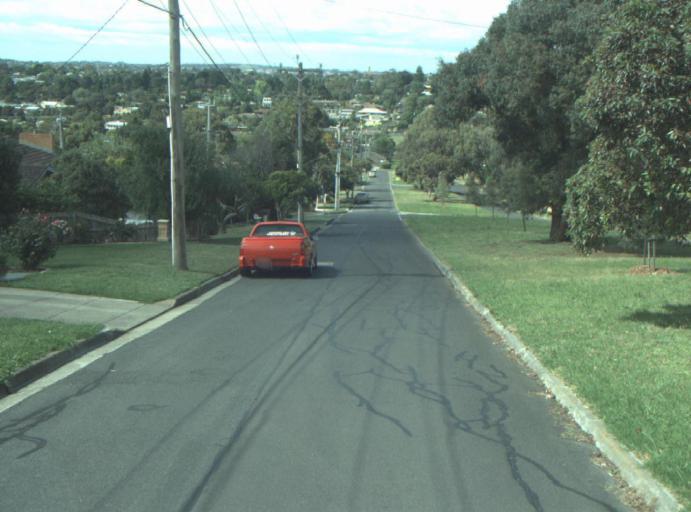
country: AU
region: Victoria
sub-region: Greater Geelong
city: Wandana Heights
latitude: -38.1641
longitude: 144.3154
